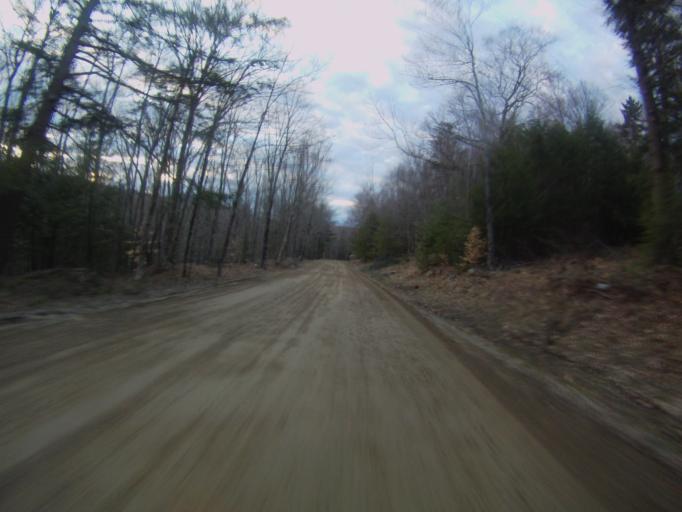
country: US
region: Vermont
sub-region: Rutland County
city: Brandon
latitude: 43.9435
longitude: -73.0230
